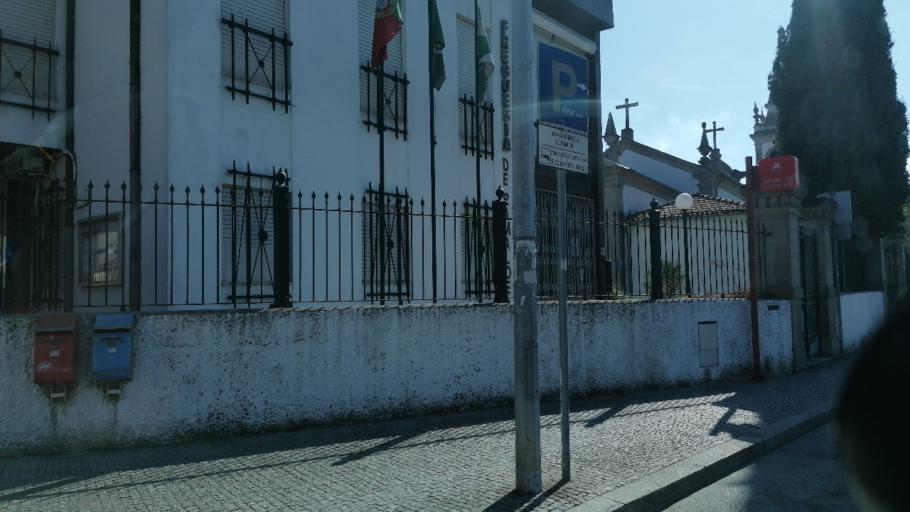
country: PT
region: Porto
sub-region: Matosinhos
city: Senhora da Hora
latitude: 41.1685
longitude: -8.6475
